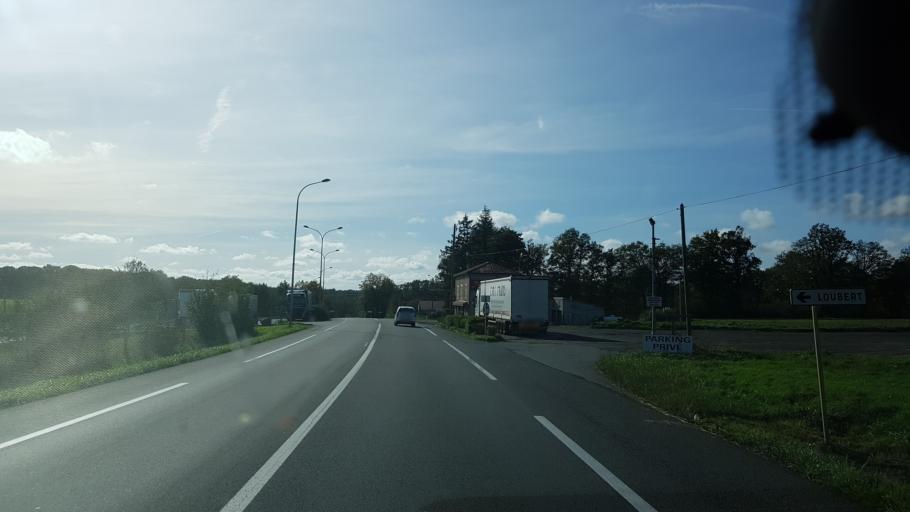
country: FR
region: Poitou-Charentes
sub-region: Departement de la Charente
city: Loubert
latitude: 45.9458
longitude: 0.5531
